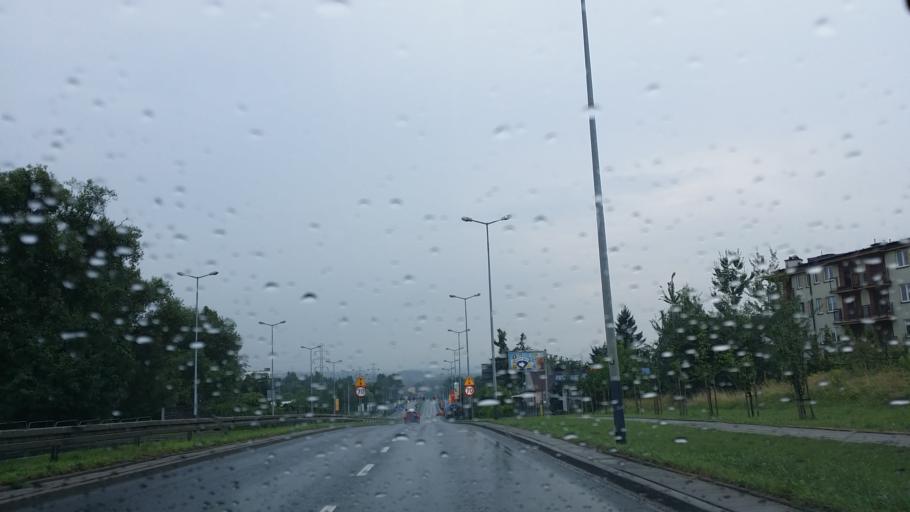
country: PL
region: Lesser Poland Voivodeship
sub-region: Krakow
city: Krakow
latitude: 50.0220
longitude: 19.9458
